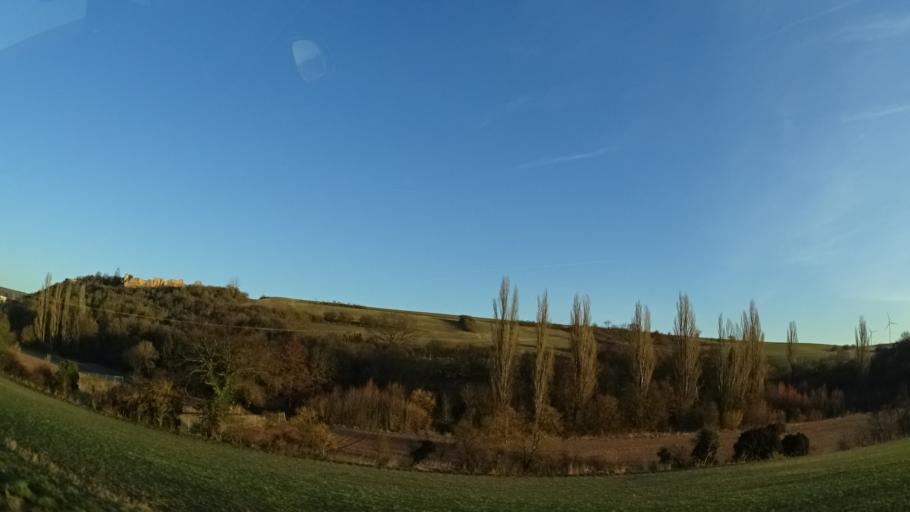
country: DE
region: Rheinland-Pfalz
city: Bolanden
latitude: 49.6368
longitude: 8.0170
